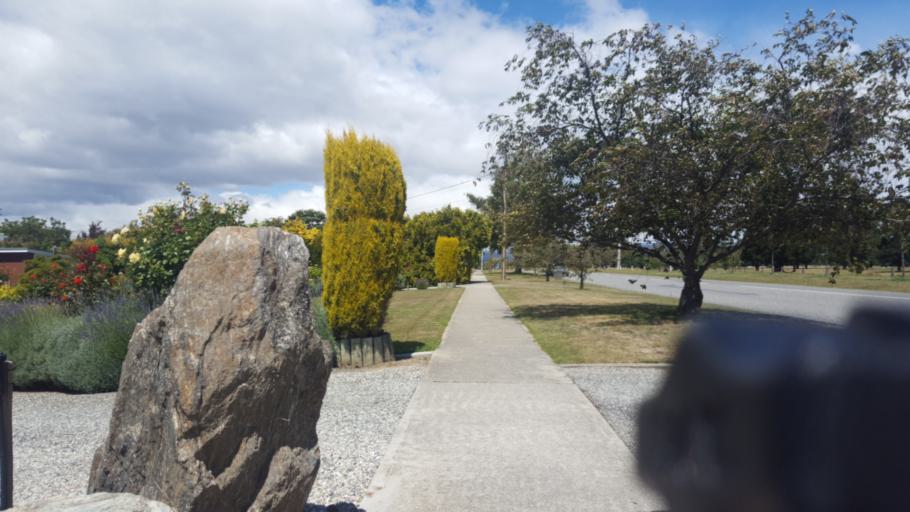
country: NZ
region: Otago
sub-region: Queenstown-Lakes District
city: Wanaka
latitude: -45.1920
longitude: 169.3234
